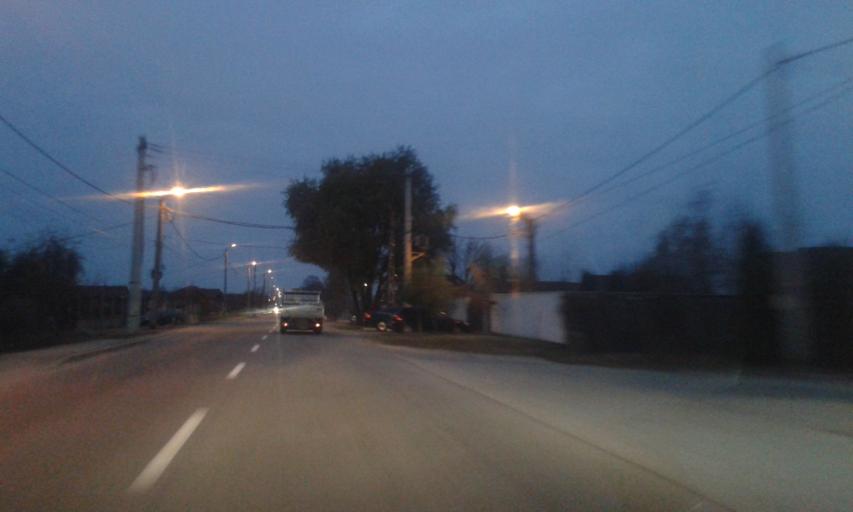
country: RO
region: Gorj
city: Targu Jiu
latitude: 45.0504
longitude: 23.2621
